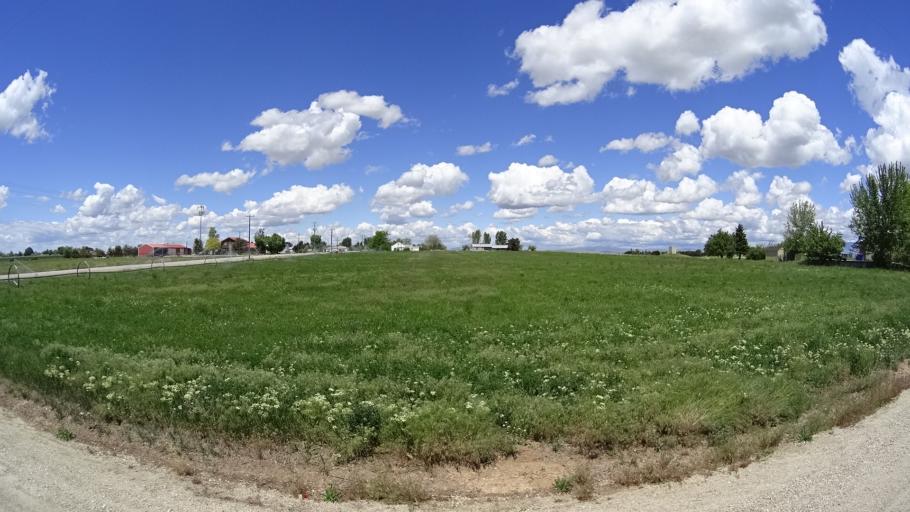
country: US
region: Idaho
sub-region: Ada County
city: Meridian
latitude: 43.5830
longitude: -116.4531
